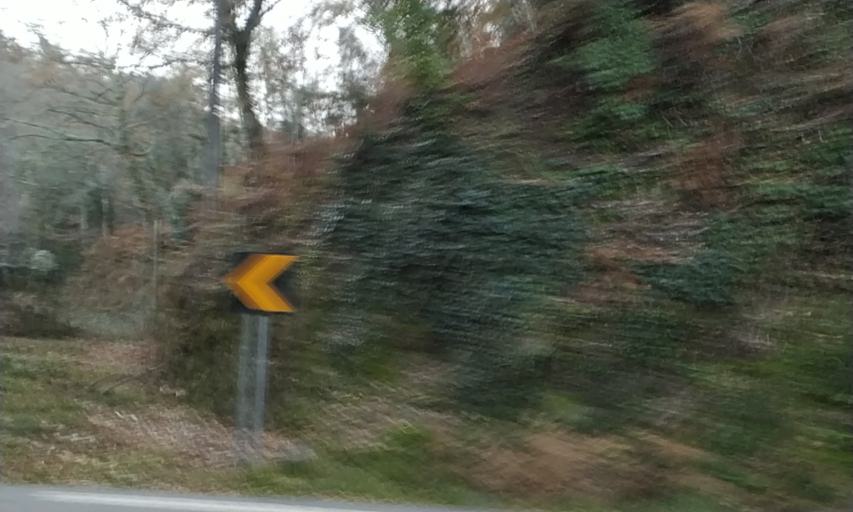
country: PT
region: Vila Real
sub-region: Mondim de Basto
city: Mondim de Basto
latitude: 41.4594
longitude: -7.9647
